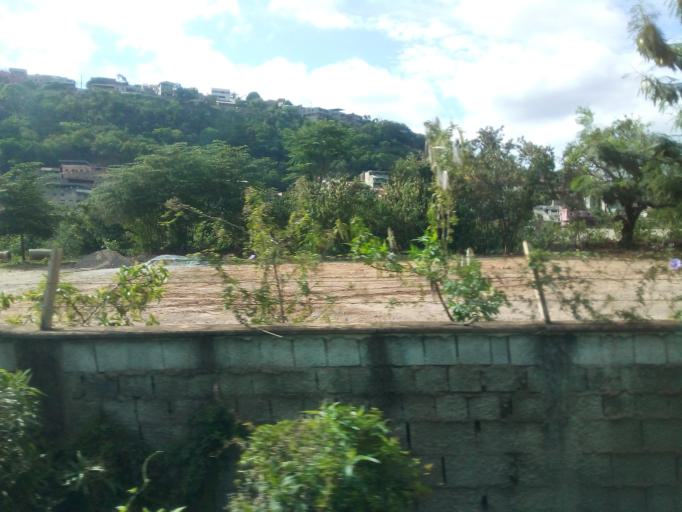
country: BR
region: Minas Gerais
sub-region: Belo Horizonte
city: Belo Horizonte
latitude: -19.8835
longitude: -43.8607
